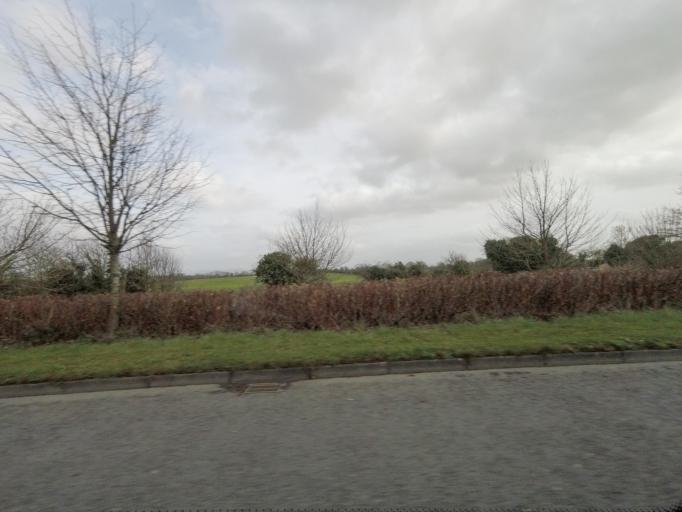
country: IE
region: Leinster
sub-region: Kildare
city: Kilcullen
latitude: 53.1244
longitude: -6.7507
